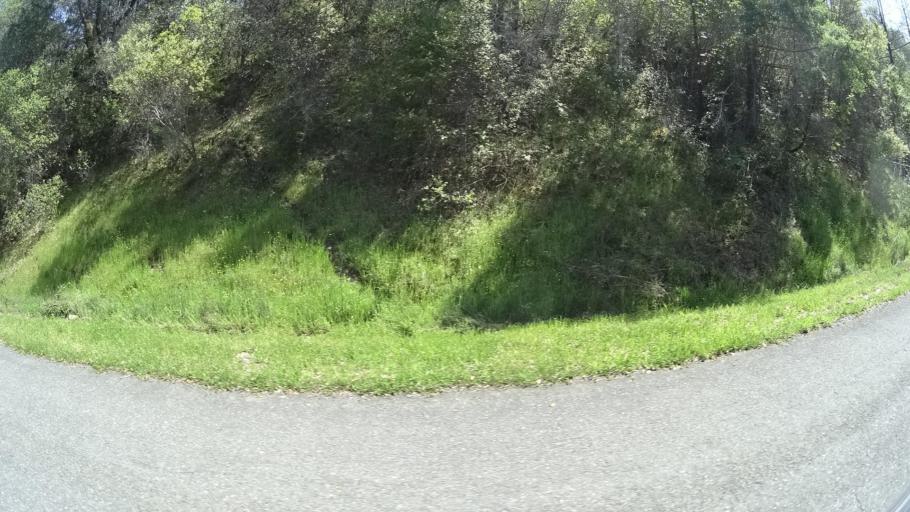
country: US
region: California
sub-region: Humboldt County
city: Redway
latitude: 40.2358
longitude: -123.6372
